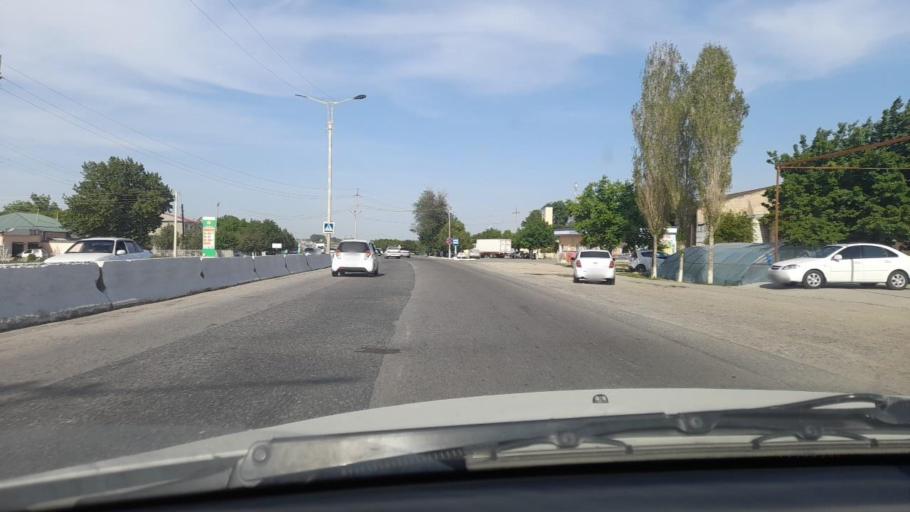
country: UZ
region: Samarqand
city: Bulung'ur
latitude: 39.7711
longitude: 67.2745
